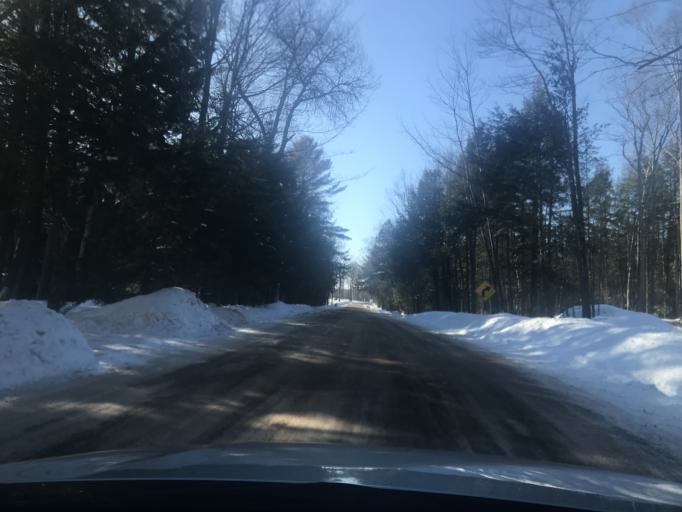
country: US
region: Wisconsin
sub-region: Marinette County
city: Marinette
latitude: 45.1377
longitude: -87.6707
